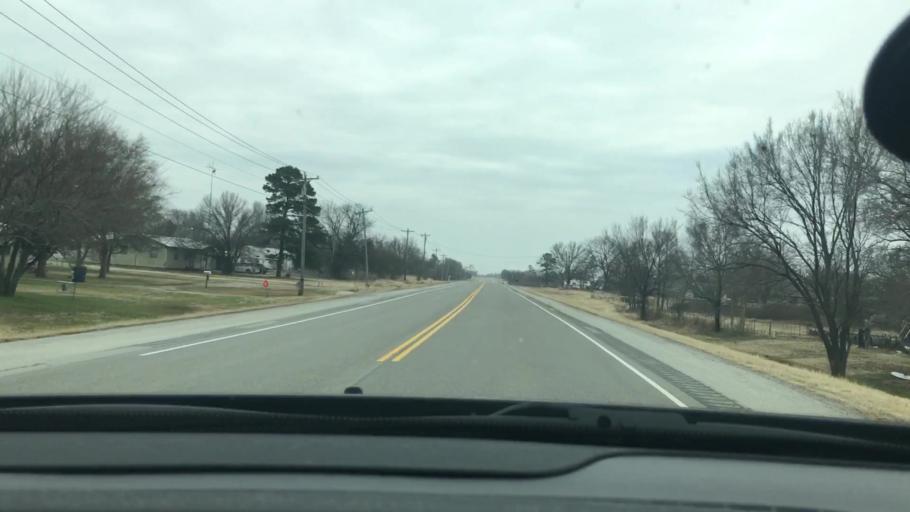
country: US
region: Oklahoma
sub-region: Carter County
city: Healdton
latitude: 34.4050
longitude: -97.5089
